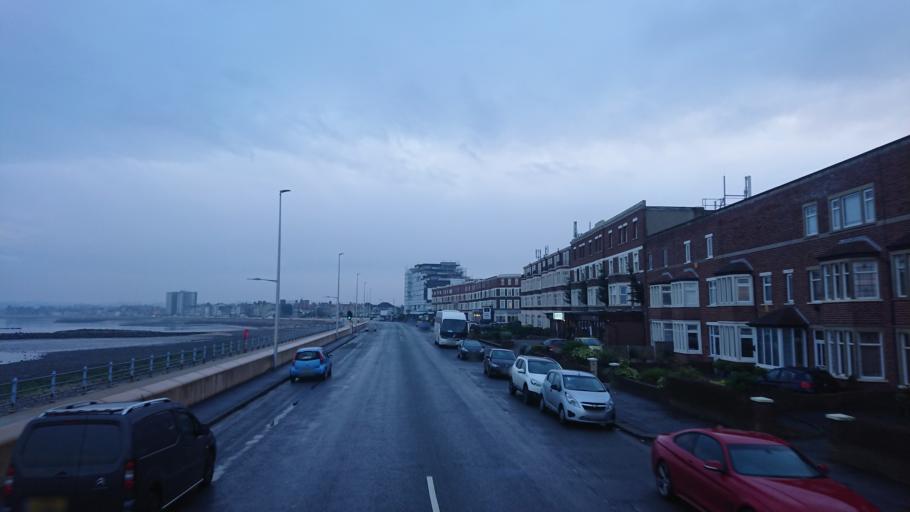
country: GB
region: England
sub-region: Lancashire
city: Morecambe
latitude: 54.0772
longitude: -2.8531
